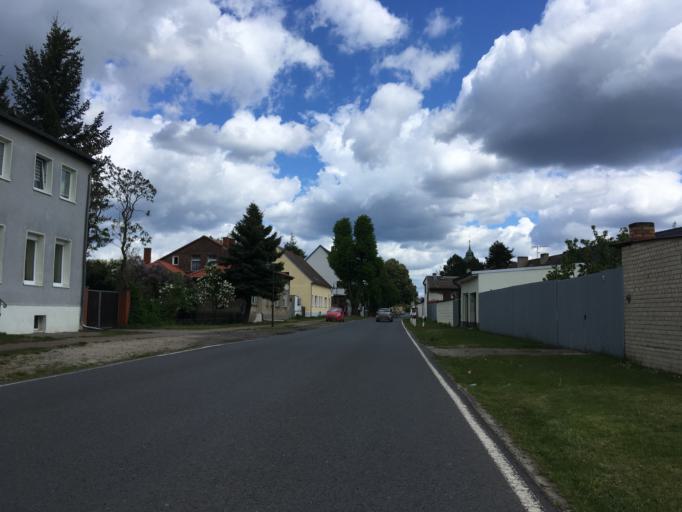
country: DE
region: Brandenburg
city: Marienwerder
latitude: 52.9044
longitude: 13.5270
